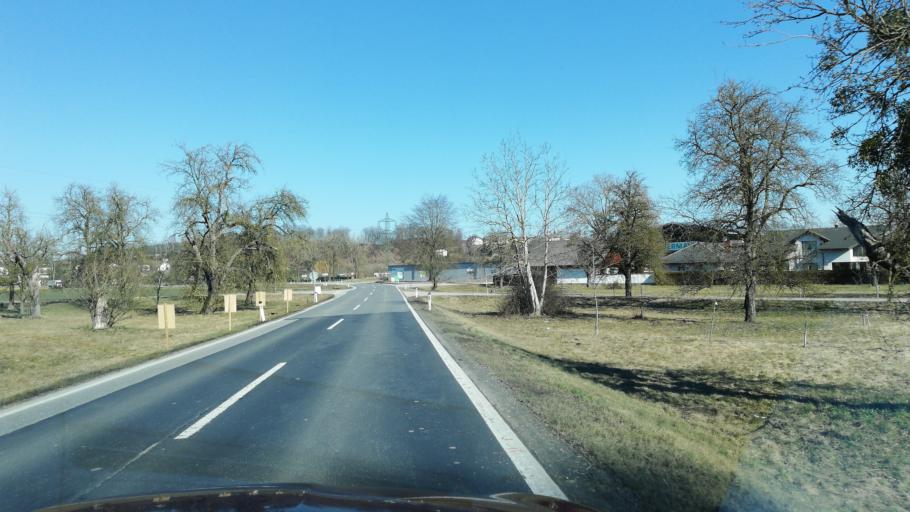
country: AT
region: Upper Austria
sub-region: Politischer Bezirk Vocklabruck
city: Schwanenstadt
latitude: 48.0578
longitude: 13.7679
